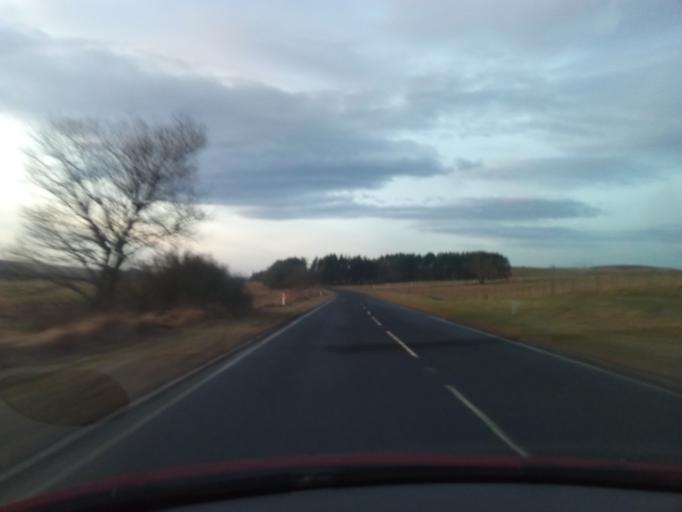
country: GB
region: England
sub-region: Northumberland
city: Otterburn
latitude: 55.2342
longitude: -2.1921
